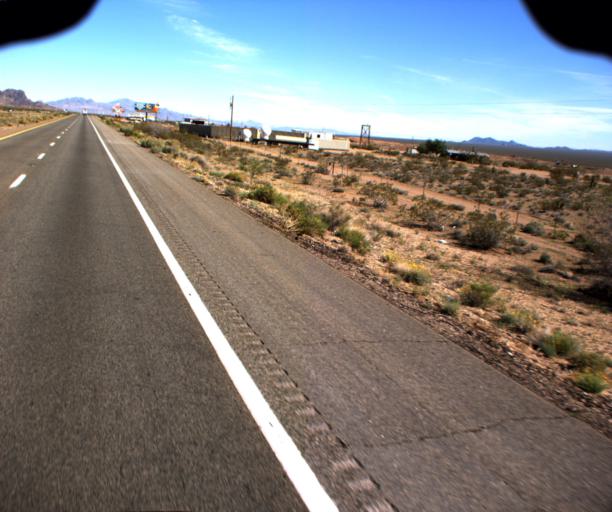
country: US
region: Arizona
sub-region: Mohave County
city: Dolan Springs
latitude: 35.7179
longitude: -114.4841
